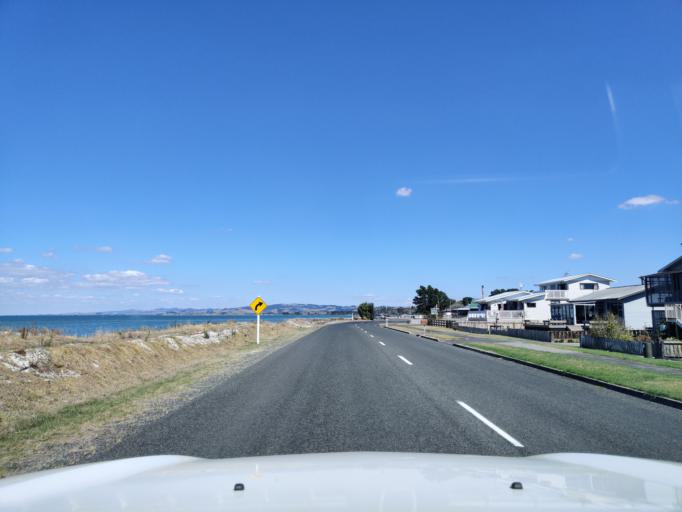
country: NZ
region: Waikato
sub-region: Thames-Coromandel District
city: Thames
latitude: -37.1079
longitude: 175.2991
